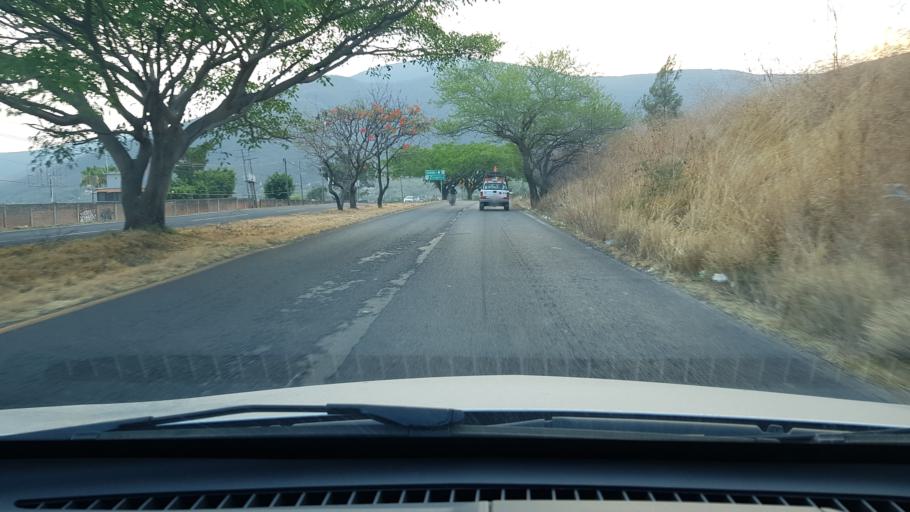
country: MX
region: Morelos
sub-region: Jiutepec
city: Independencia
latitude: 18.8595
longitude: -99.0994
